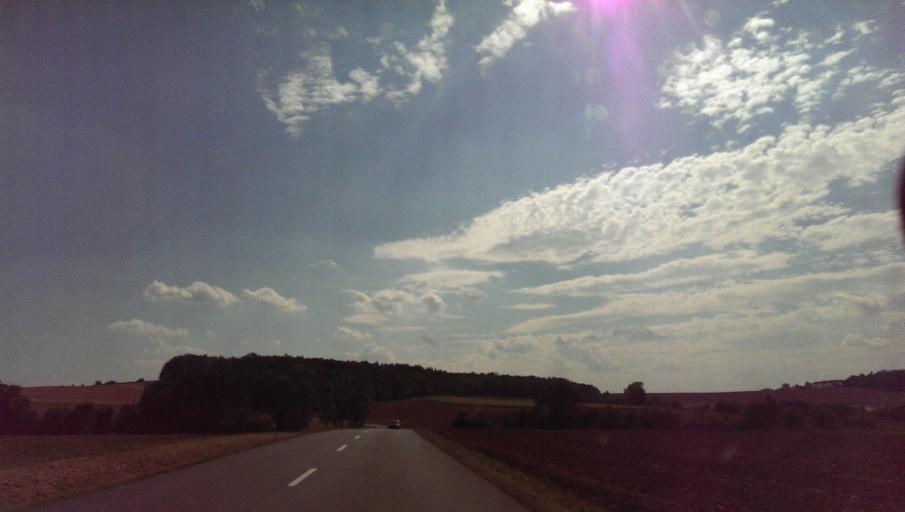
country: CZ
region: Zlin
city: Tlumacov
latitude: 49.2672
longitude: 17.5473
